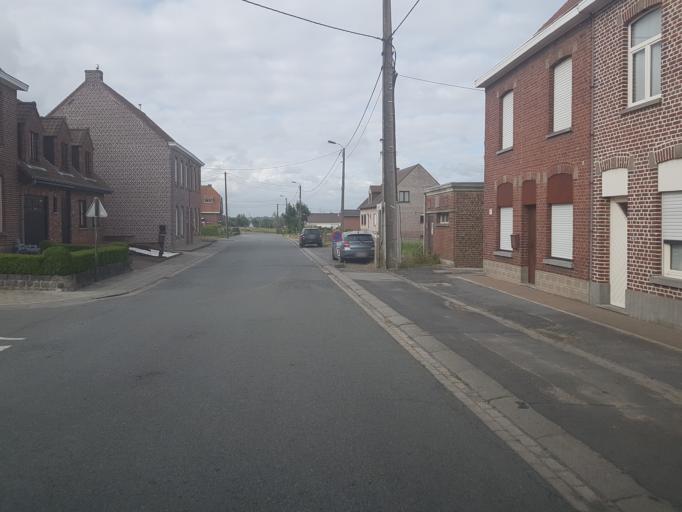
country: BE
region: Flanders
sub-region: Provincie West-Vlaanderen
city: Waregem
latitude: 50.8354
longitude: 3.4162
